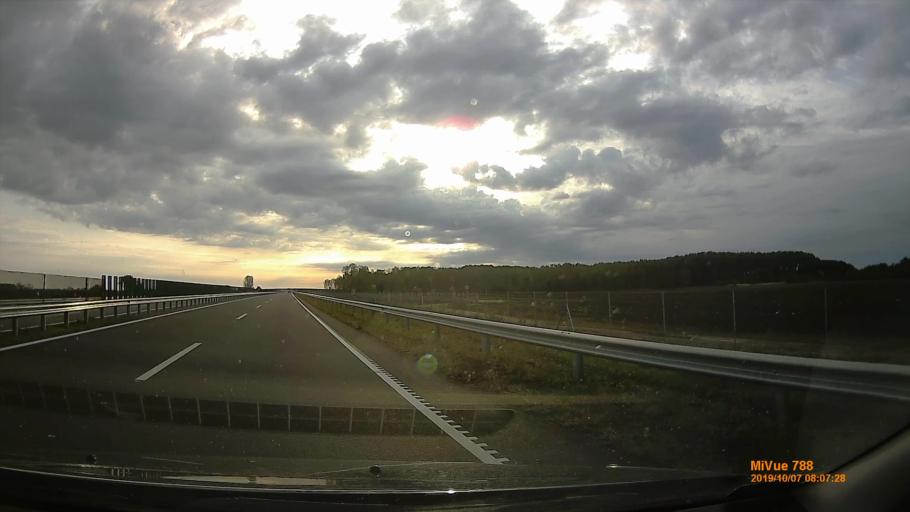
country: HU
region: Jasz-Nagykun-Szolnok
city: Cserkeszolo
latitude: 46.8856
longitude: 20.1946
